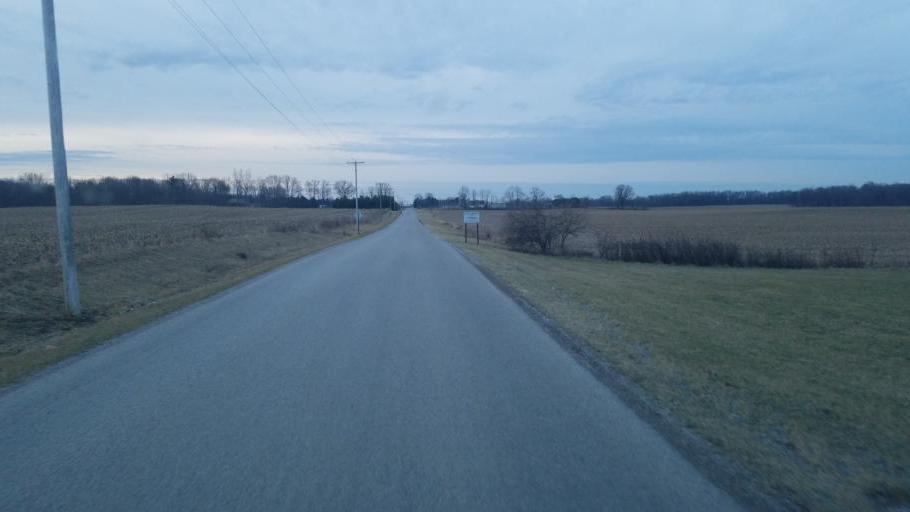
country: US
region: Ohio
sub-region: Morrow County
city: Mount Gilead
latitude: 40.5437
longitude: -82.8538
